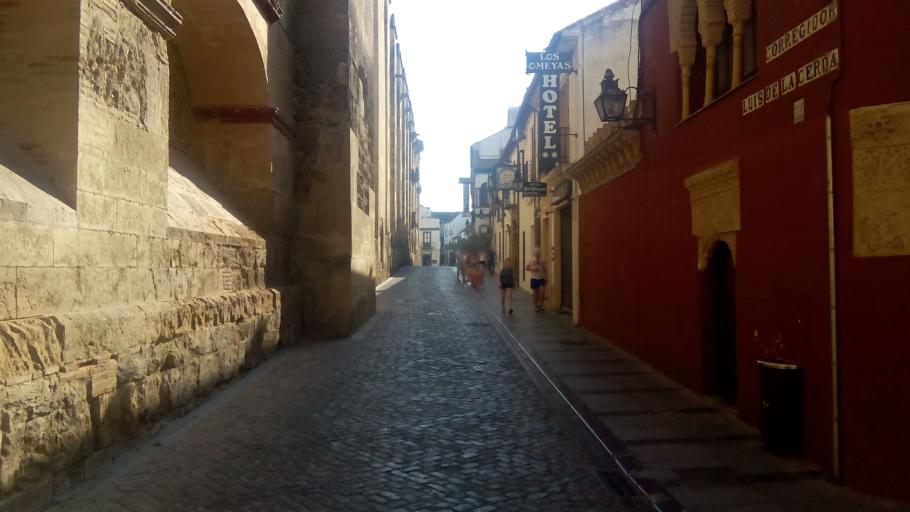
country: ES
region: Andalusia
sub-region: Province of Cordoba
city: Cordoba
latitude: 37.8782
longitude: -4.7795
